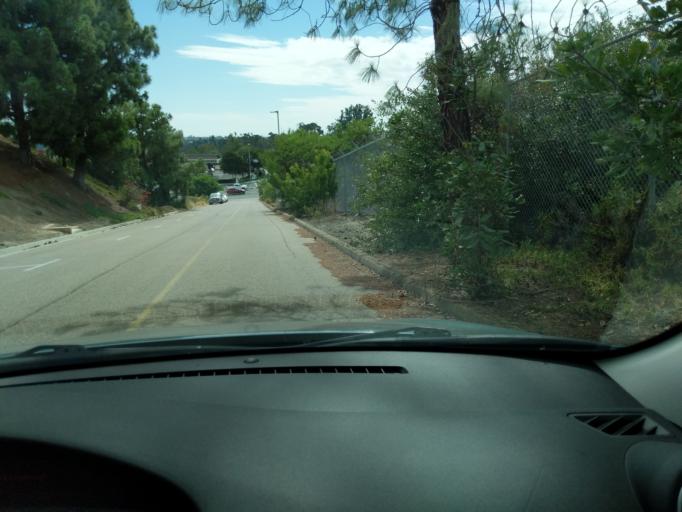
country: US
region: California
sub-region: San Diego County
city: San Diego
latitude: 32.8097
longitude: -117.1222
